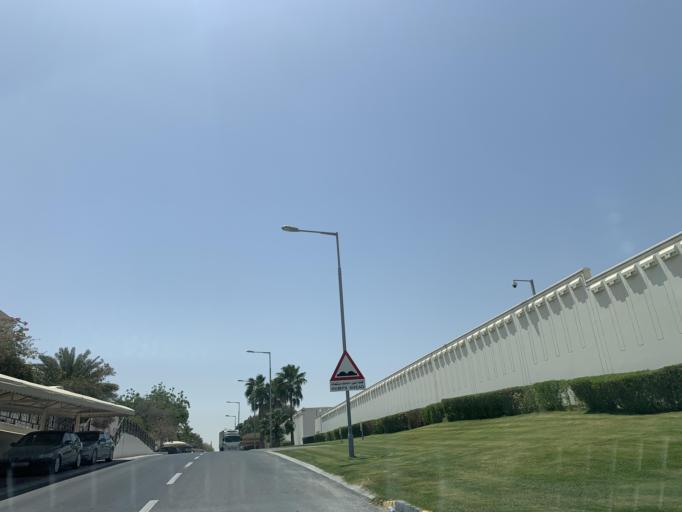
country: BH
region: Northern
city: Ar Rifa'
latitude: 26.1461
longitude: 50.5545
